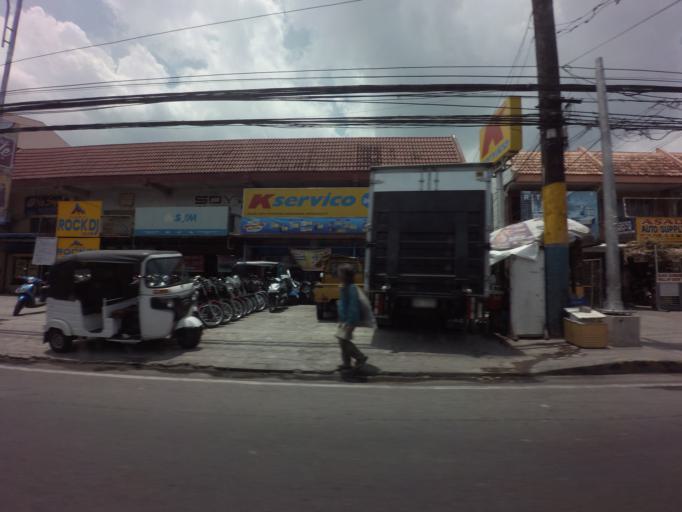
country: PH
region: Calabarzon
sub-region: Province of Laguna
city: San Pedro
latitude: 14.4057
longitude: 121.0469
